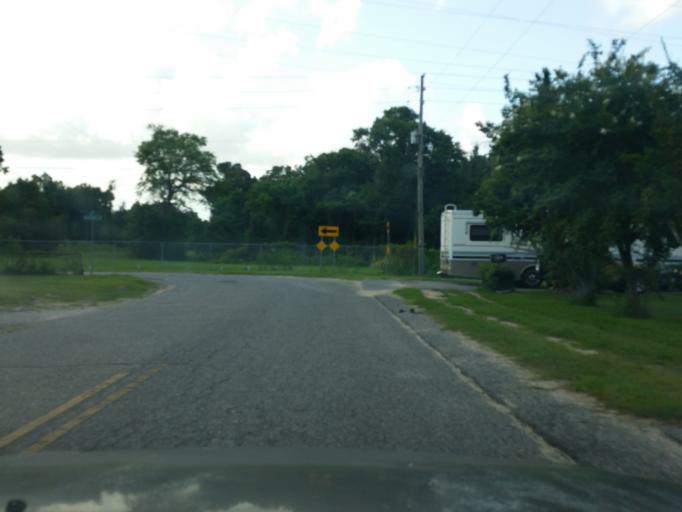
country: US
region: Florida
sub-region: Escambia County
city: Ferry Pass
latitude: 30.4990
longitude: -87.2127
